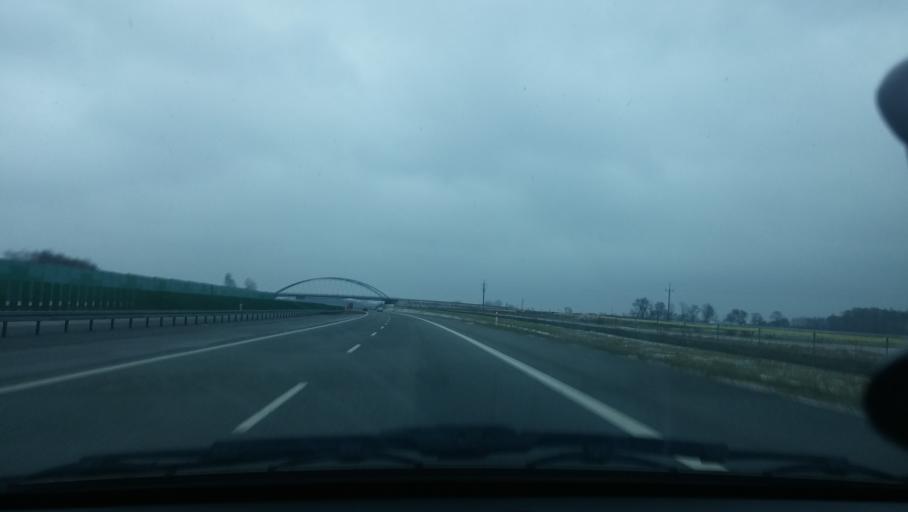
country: PL
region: Masovian Voivodeship
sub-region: Powiat minski
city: Jakubow
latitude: 52.2069
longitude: 21.6694
